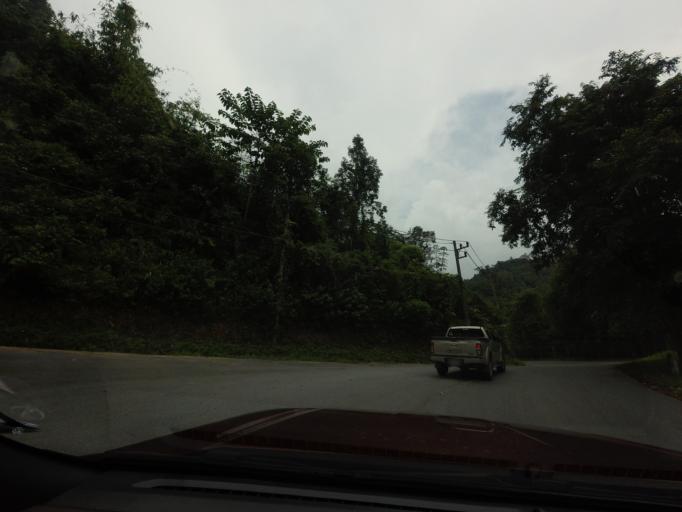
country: TH
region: Yala
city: Than To
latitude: 6.1580
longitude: 101.2793
